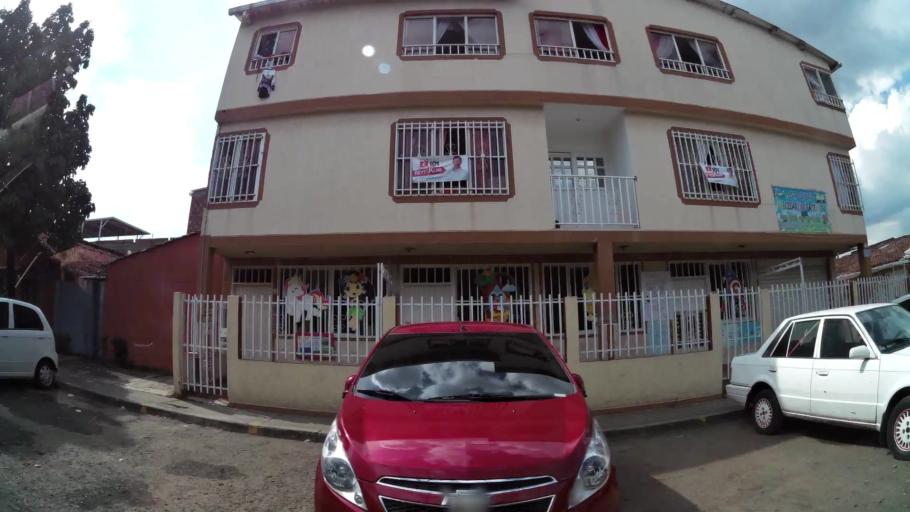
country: CO
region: Valle del Cauca
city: Cali
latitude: 3.3968
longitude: -76.5138
